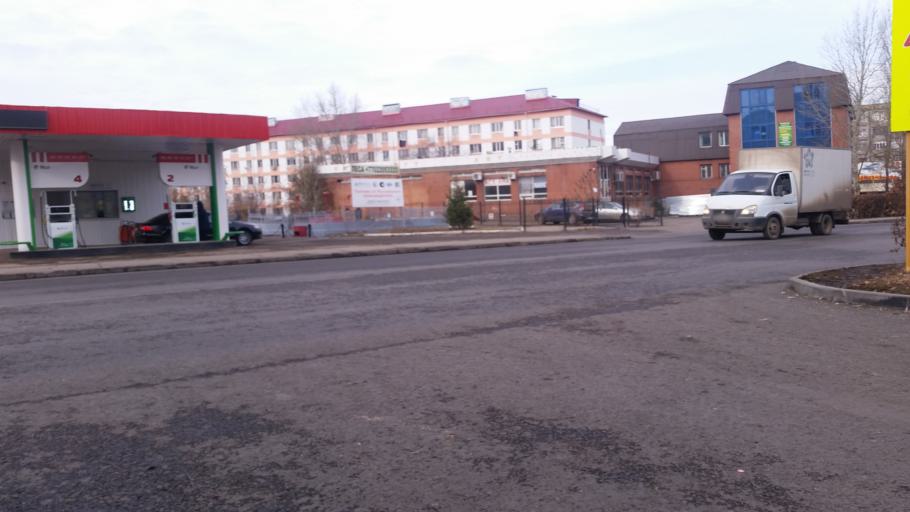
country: KZ
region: Astana Qalasy
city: Astana
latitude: 51.1523
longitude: 71.4744
